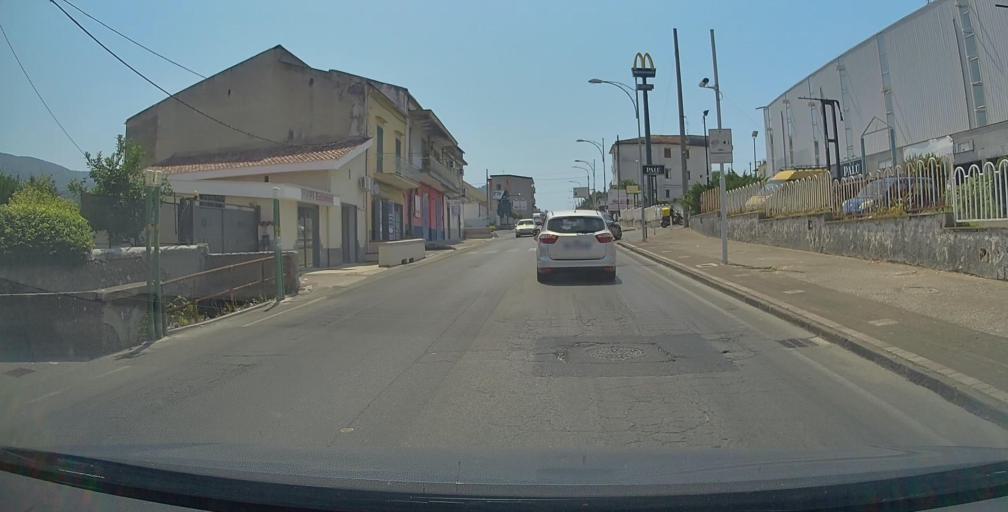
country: IT
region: Campania
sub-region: Provincia di Salerno
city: Nocera Superiore
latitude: 40.7288
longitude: 14.6899
